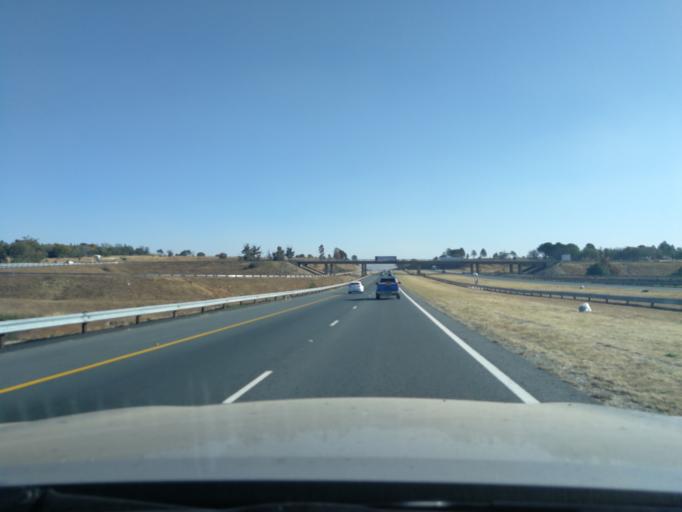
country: ZA
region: Gauteng
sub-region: West Rand District Municipality
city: Muldersdriseloop
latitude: -26.0190
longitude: 27.8633
